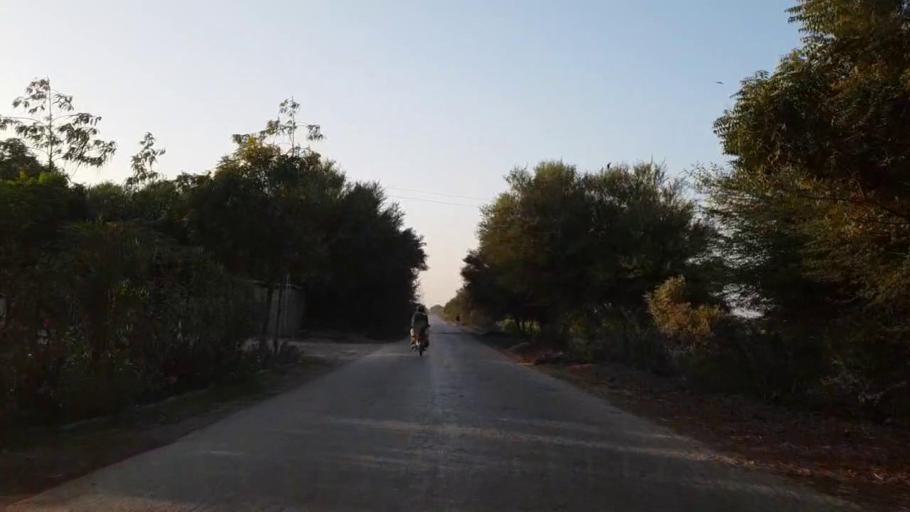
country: PK
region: Sindh
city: Chambar
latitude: 25.2352
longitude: 68.6997
